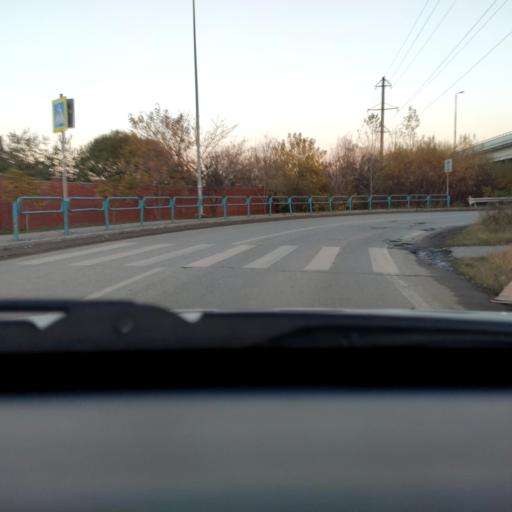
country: RU
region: Perm
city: Kondratovo
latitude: 58.0007
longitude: 56.1231
